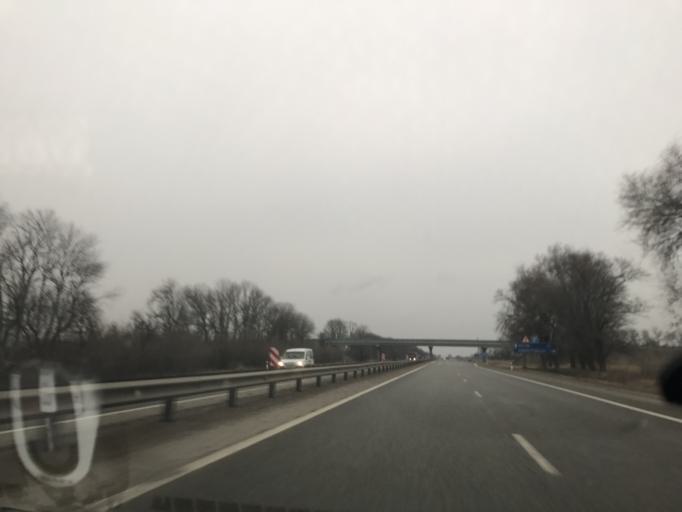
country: RU
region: Krasnodarskiy
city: Pavlovskaya
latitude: 46.2039
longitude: 39.8315
